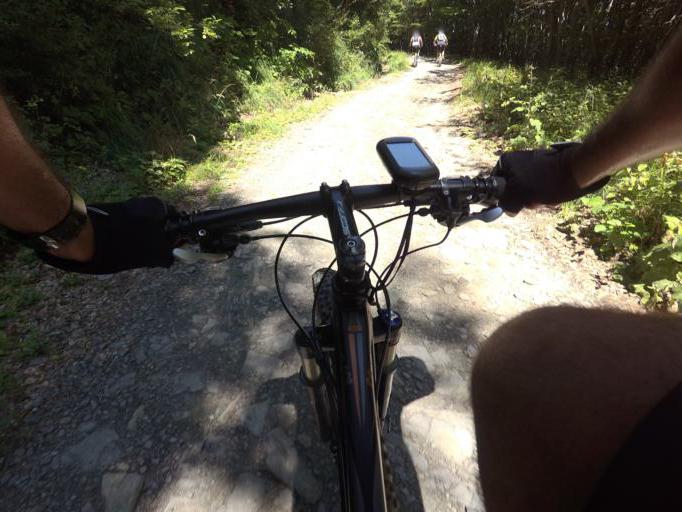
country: IT
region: Emilia-Romagna
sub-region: Provincia di Modena
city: Montecreto
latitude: 44.2262
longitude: 10.7257
